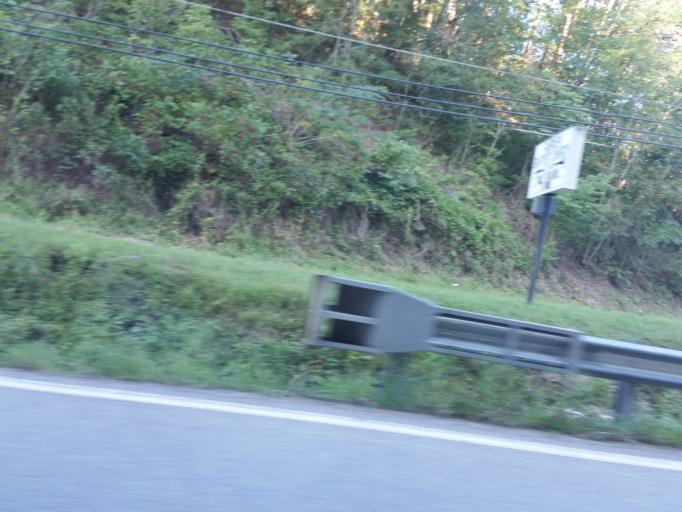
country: US
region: Tennessee
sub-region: Union County
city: Luttrell
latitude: 36.2439
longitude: -83.7453
